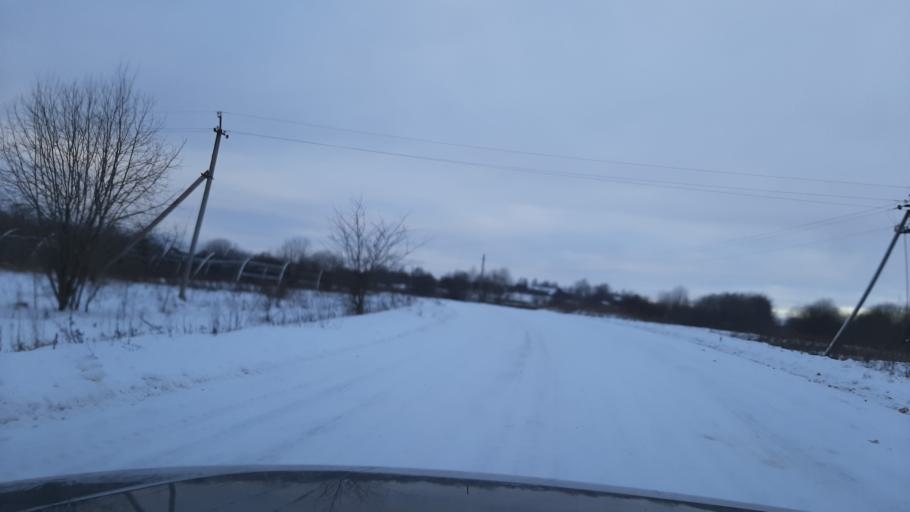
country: RU
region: Kostroma
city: Volgorechensk
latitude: 57.4489
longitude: 40.9768
